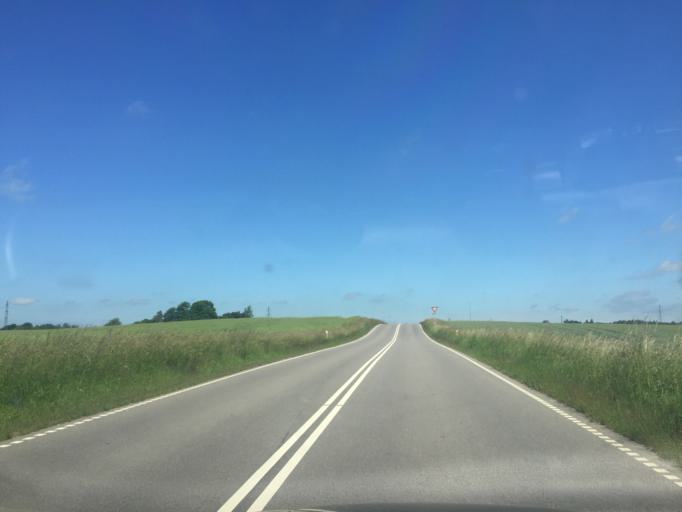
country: DK
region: Capital Region
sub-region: Hoje-Taastrup Kommune
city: Flong
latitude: 55.6705
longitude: 12.2102
